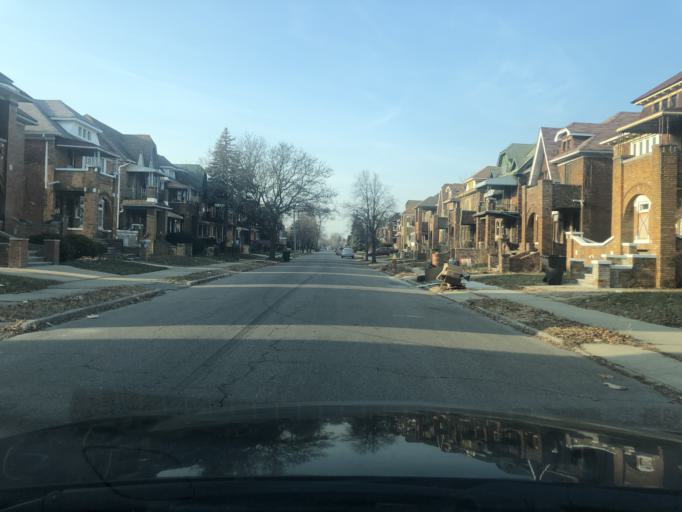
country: US
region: Michigan
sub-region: Wayne County
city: Highland Park
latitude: 42.3881
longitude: -83.1308
